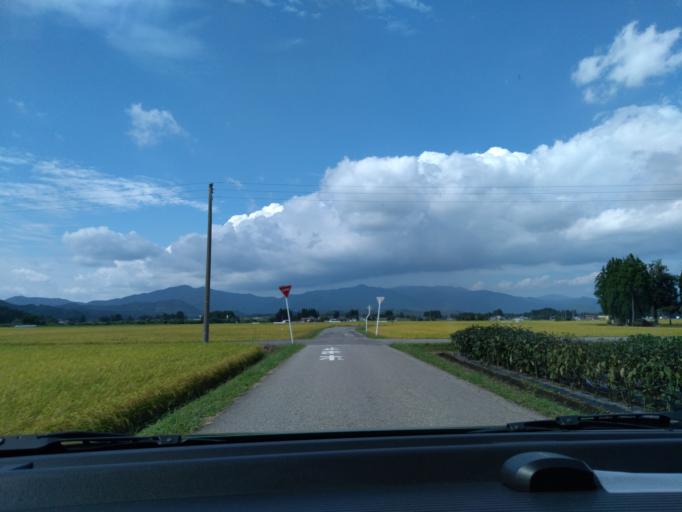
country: JP
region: Akita
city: Kakunodatemachi
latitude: 39.6052
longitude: 140.5857
